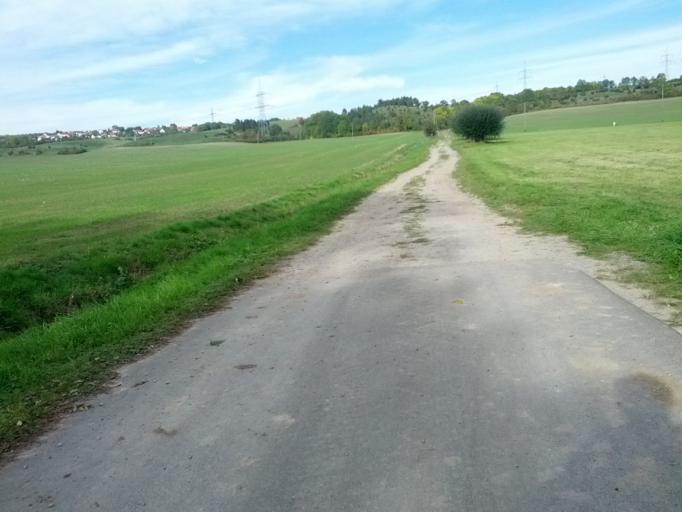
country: DE
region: Thuringia
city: Krauthausen
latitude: 51.0212
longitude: 10.2943
